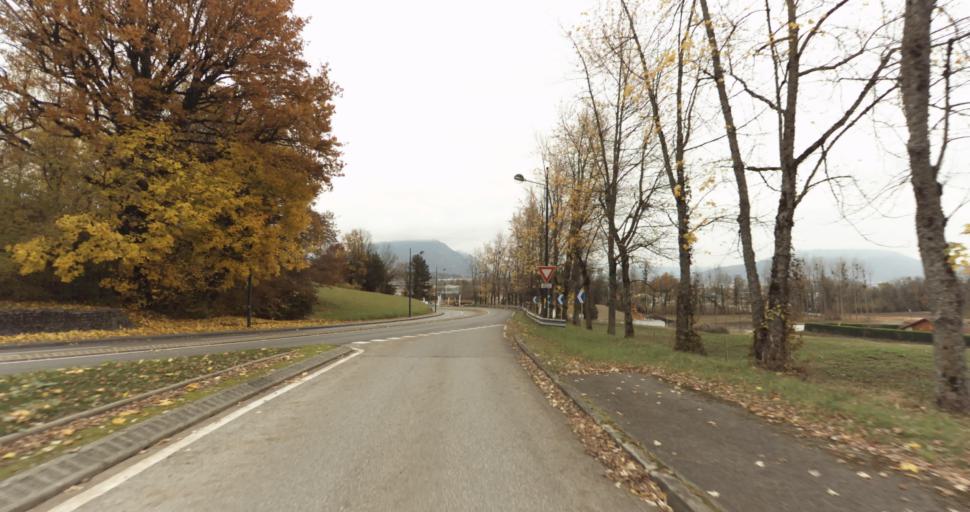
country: FR
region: Rhone-Alpes
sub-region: Departement de la Haute-Savoie
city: Pringy
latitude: 45.9451
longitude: 6.1205
